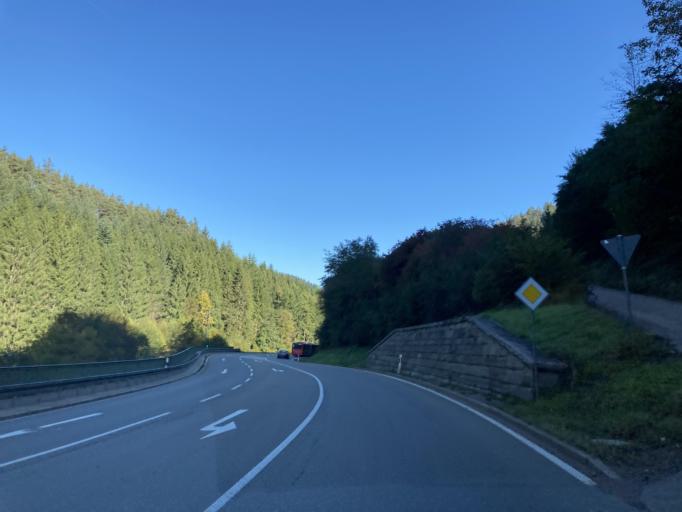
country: DE
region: Baden-Wuerttemberg
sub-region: Freiburg Region
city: Hornberg
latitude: 48.1832
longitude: 8.2313
